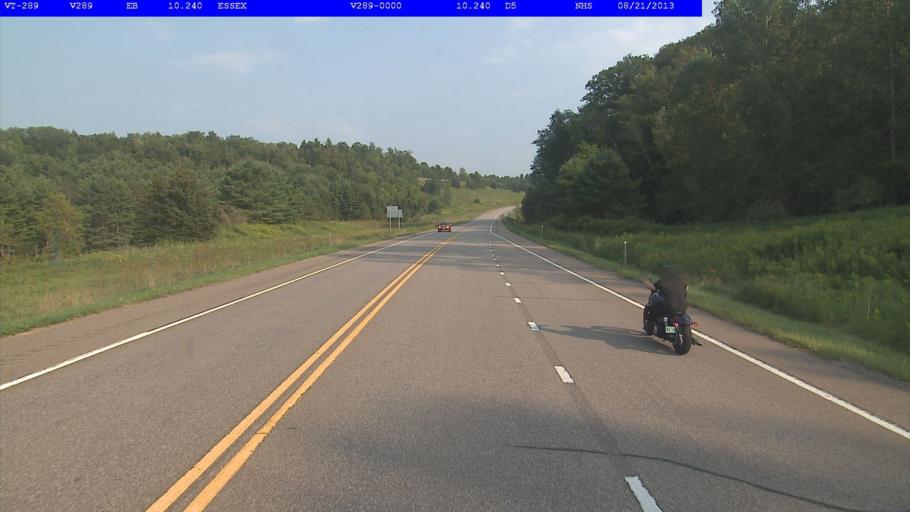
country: US
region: Vermont
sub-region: Chittenden County
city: Essex Junction
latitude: 44.5026
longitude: -73.0741
